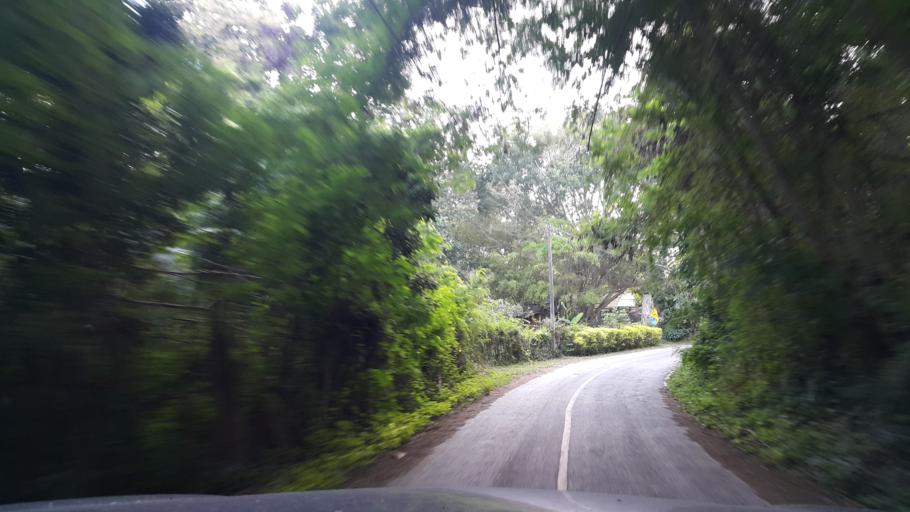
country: TH
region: Chiang Mai
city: San Sai
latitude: 18.9334
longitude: 99.0603
